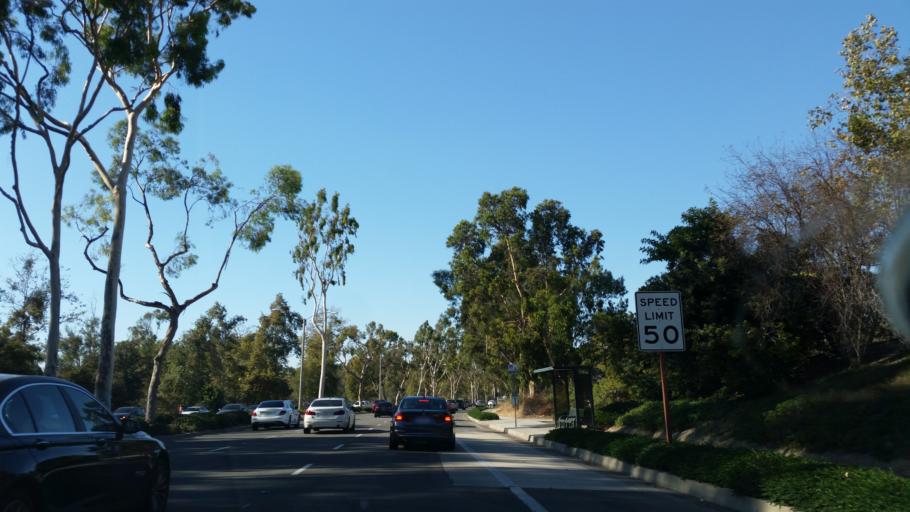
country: US
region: California
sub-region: Orange County
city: Irvine
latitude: 33.6541
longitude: -117.8268
